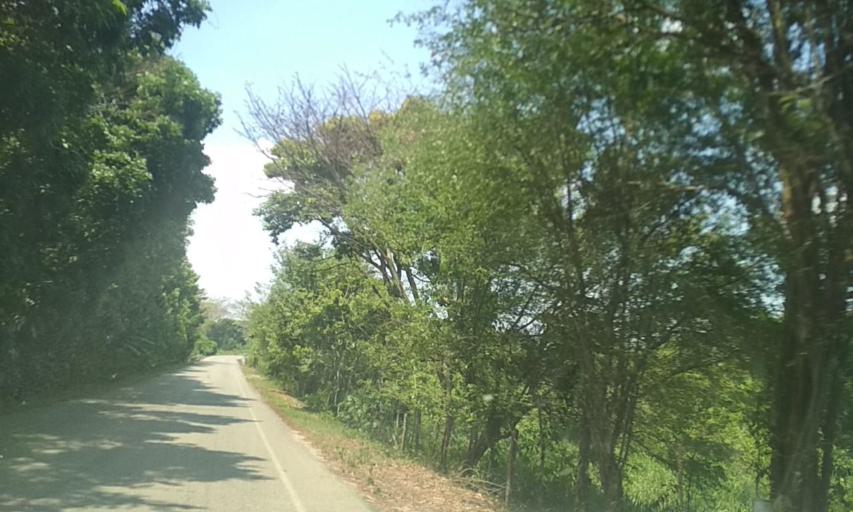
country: MX
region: Tabasco
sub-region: Huimanguillo
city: Paso de la Mina 2da. Seccion (Barrial)
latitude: 17.7785
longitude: -93.6384
